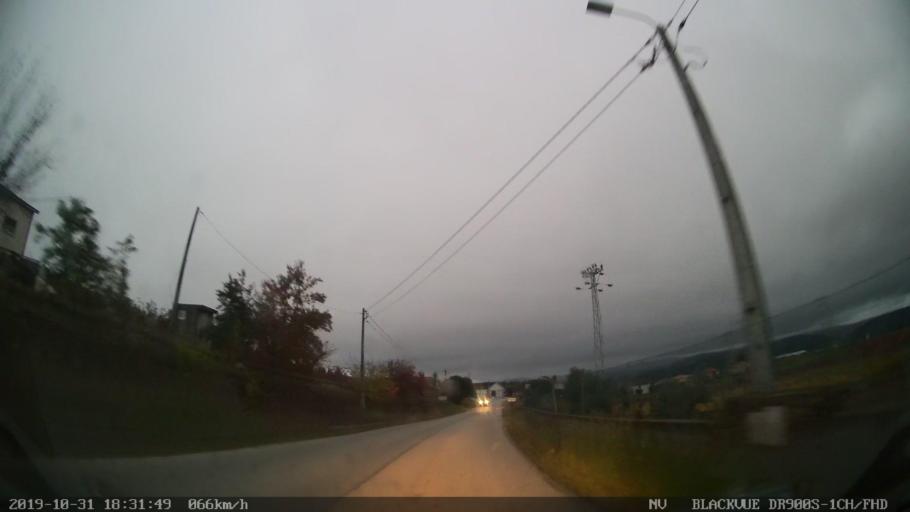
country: PT
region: Vila Real
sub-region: Sabrosa
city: Sabrosa
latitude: 41.2407
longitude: -7.5698
